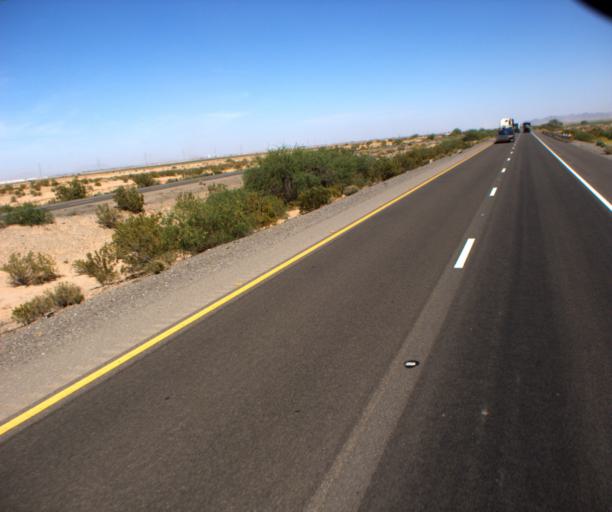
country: US
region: Arizona
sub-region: Pinal County
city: Casa Grande
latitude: 32.8281
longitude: -111.9350
